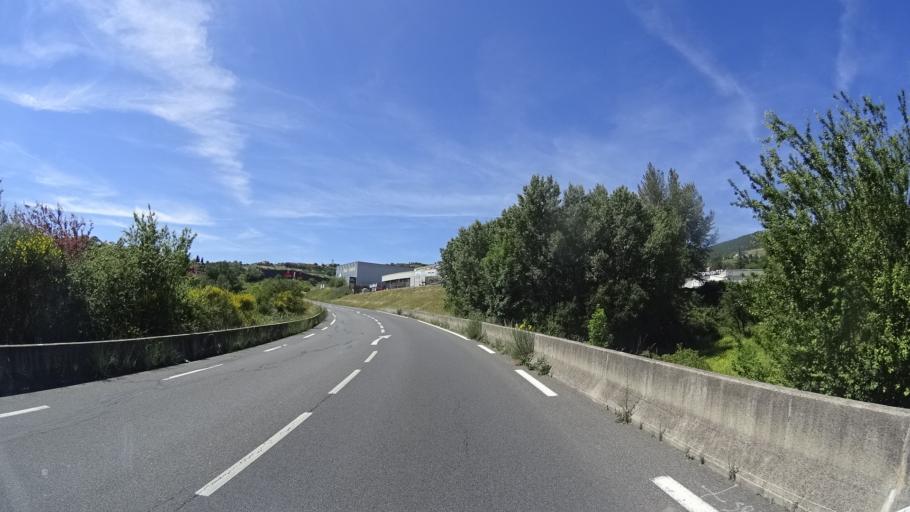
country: FR
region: Midi-Pyrenees
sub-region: Departement de l'Aveyron
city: Millau
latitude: 44.1162
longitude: 3.0740
